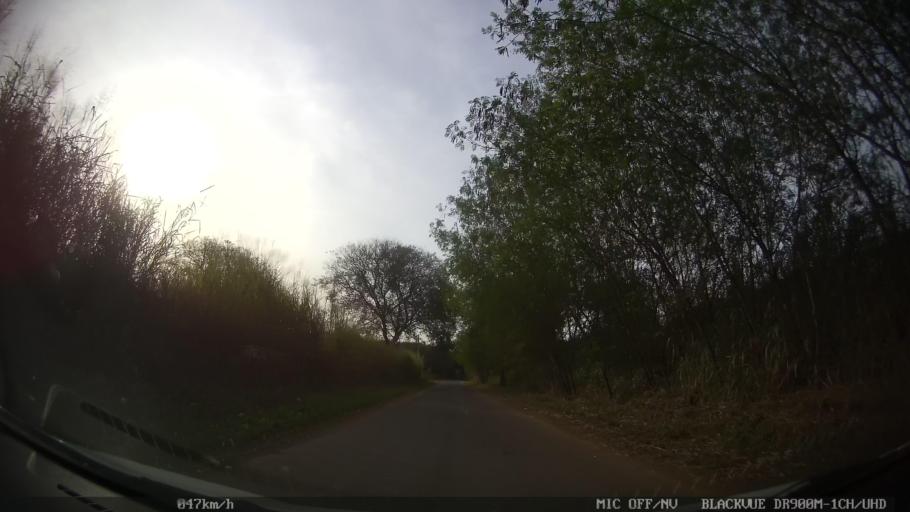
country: BR
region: Sao Paulo
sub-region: Piracicaba
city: Piracicaba
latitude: -22.7010
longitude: -47.5880
